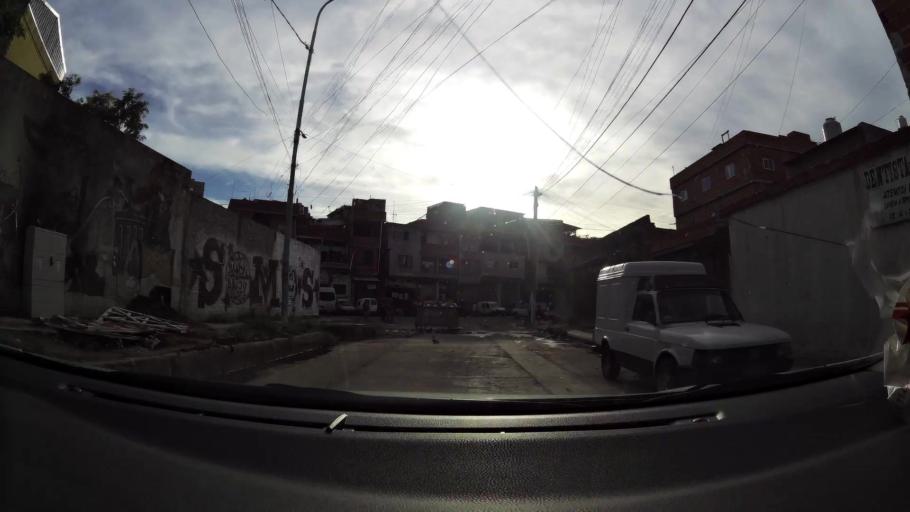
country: AR
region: Buenos Aires F.D.
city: Villa Lugano
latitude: -34.6470
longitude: -58.4414
